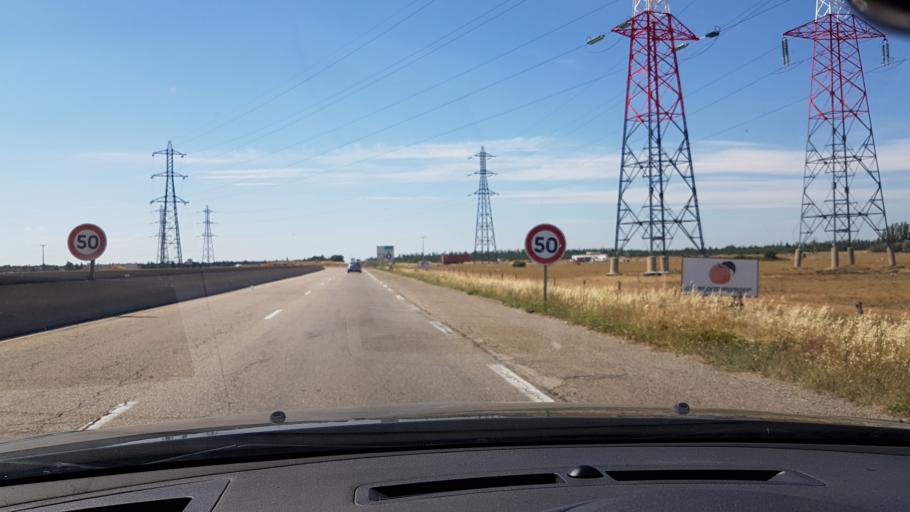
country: FR
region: Provence-Alpes-Cote d'Azur
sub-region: Departement des Bouches-du-Rhone
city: Fos-sur-Mer
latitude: 43.4845
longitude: 4.8894
